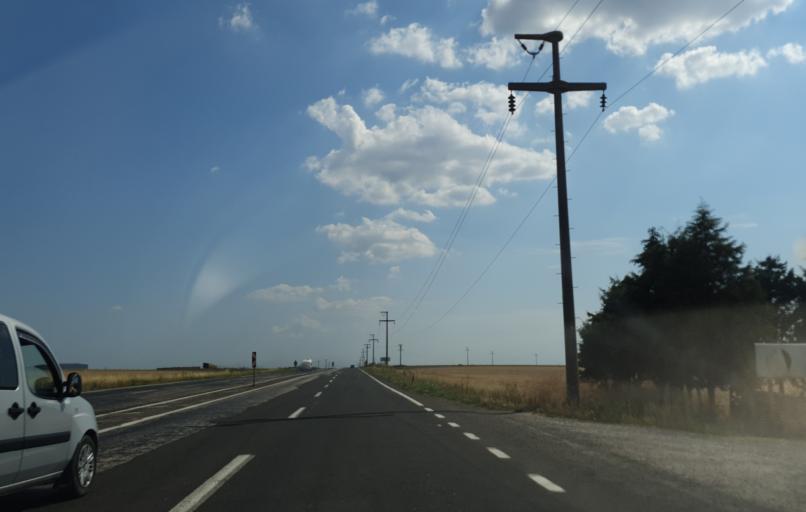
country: TR
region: Kirklareli
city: Buyukkaristiran
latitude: 41.2721
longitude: 27.5525
